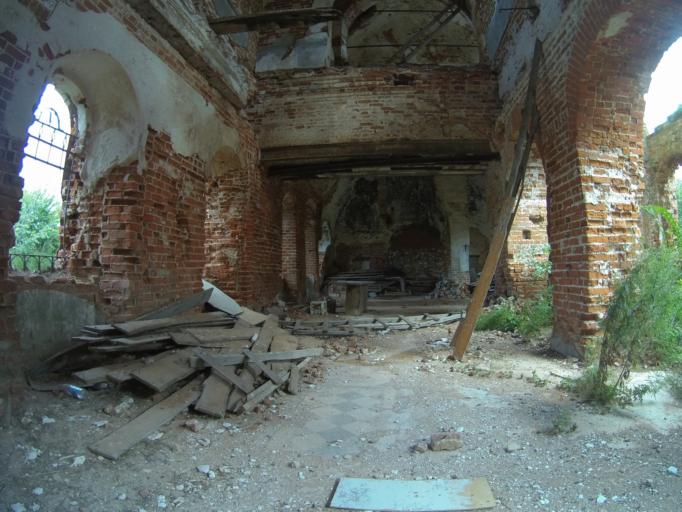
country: RU
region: Vladimir
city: Orgtrud
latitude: 56.3200
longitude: 40.6367
